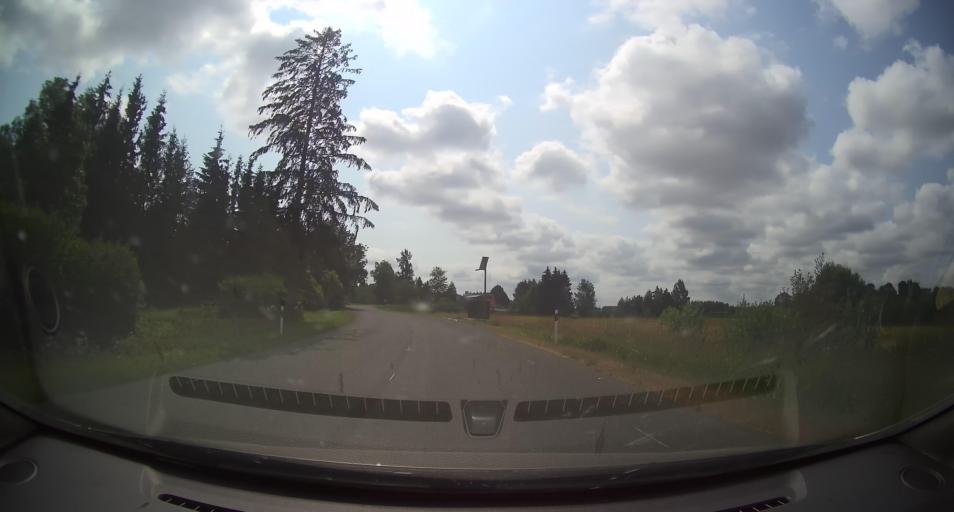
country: EE
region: Paernumaa
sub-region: Audru vald
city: Audru
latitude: 58.4962
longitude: 24.3362
